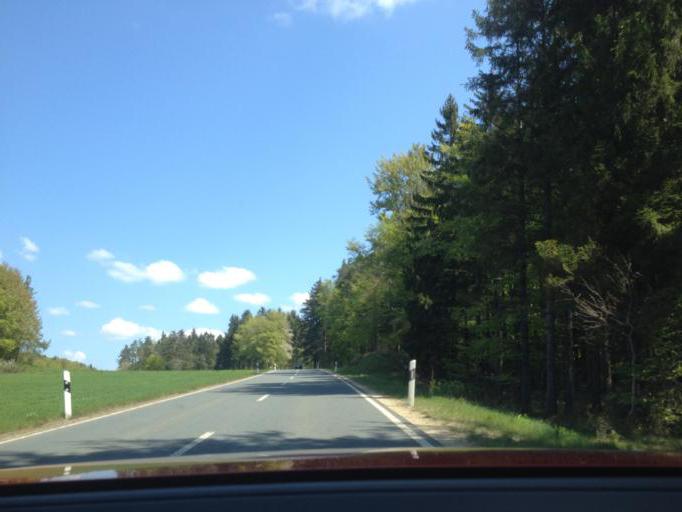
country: DE
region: Bavaria
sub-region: Regierungsbezirk Mittelfranken
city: Kirchensittenbach
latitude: 49.6255
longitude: 11.4121
